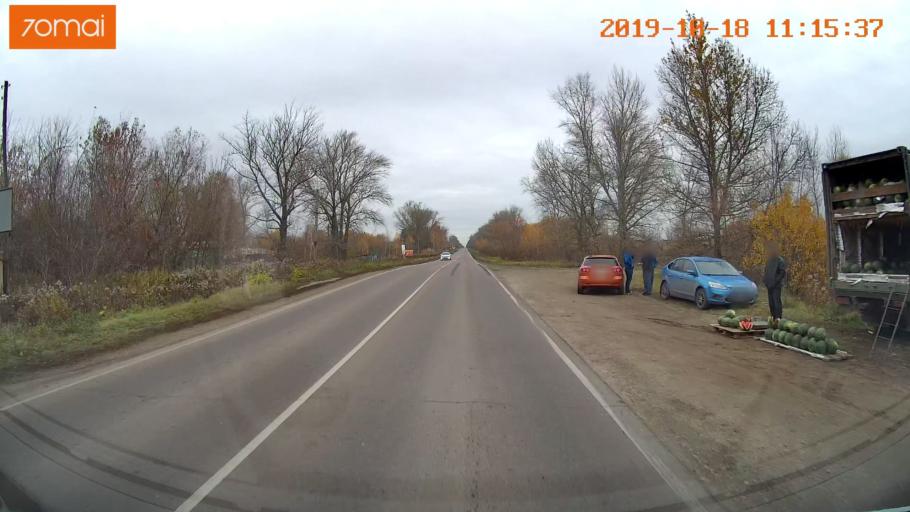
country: RU
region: Tula
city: Kimovsk
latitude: 53.9948
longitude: 38.5477
